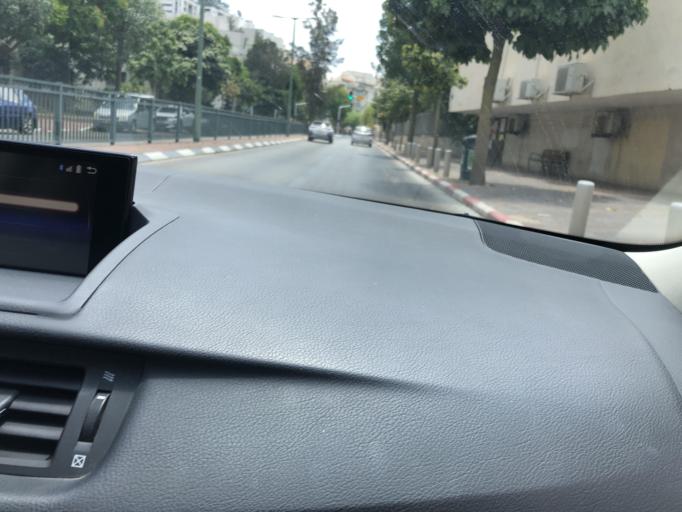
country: IL
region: Tel Aviv
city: Bene Beraq
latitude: 32.0648
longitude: 34.8329
